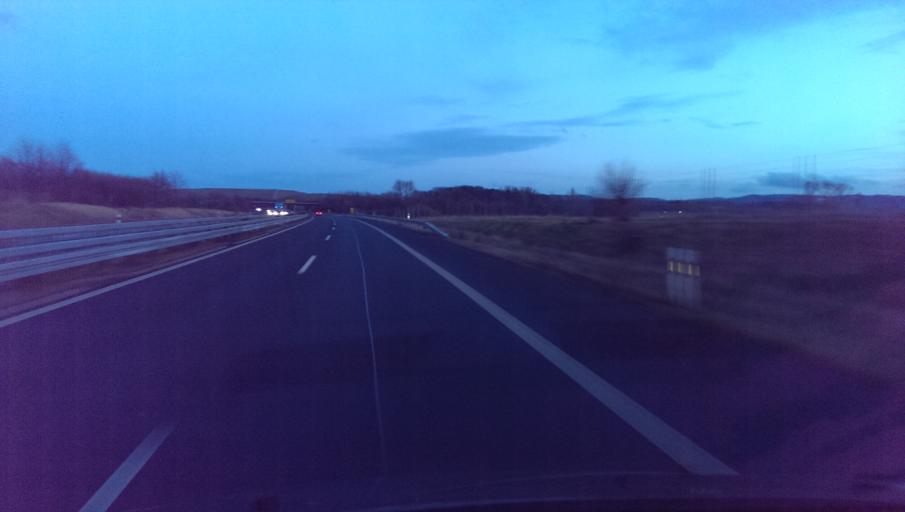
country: DE
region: Saxony-Anhalt
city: Veckenstedt
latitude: 51.8743
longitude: 10.7487
